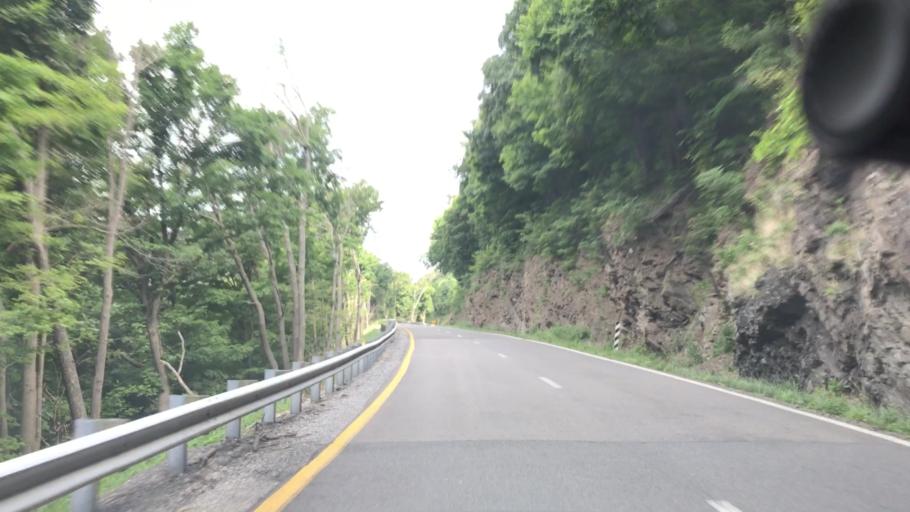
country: US
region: Virginia
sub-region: Giles County
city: Narrows
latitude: 37.3519
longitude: -80.8093
